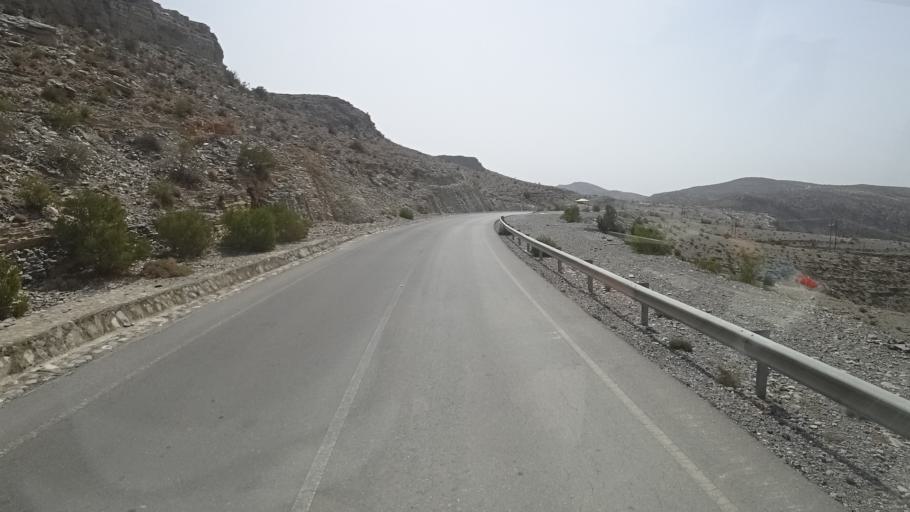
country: OM
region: Al Batinah
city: Bayt al `Awabi
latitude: 23.1662
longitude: 57.4161
